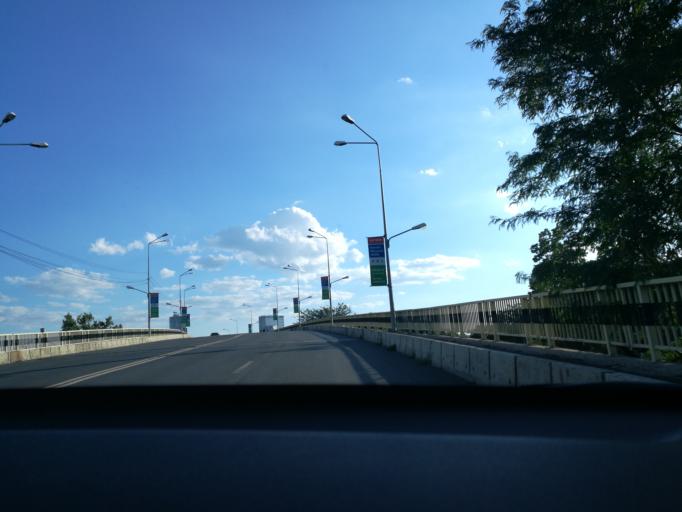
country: RO
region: Bucuresti
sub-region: Municipiul Bucuresti
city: Bucharest
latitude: 44.4881
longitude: 26.1155
